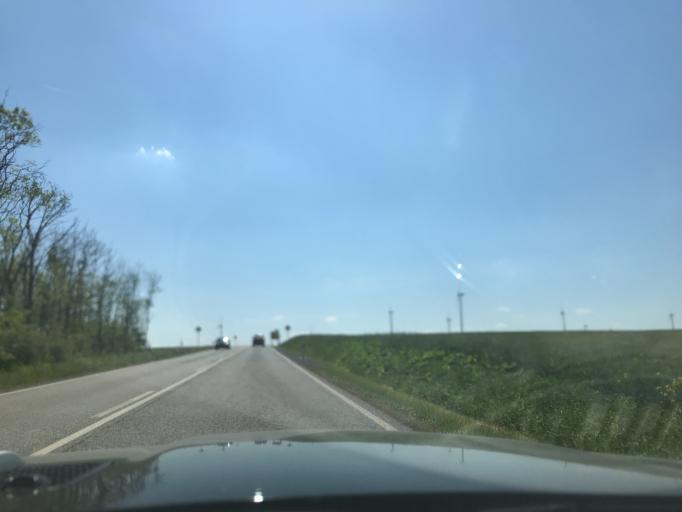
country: DE
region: Thuringia
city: Hochheim
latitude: 51.0555
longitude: 10.6519
